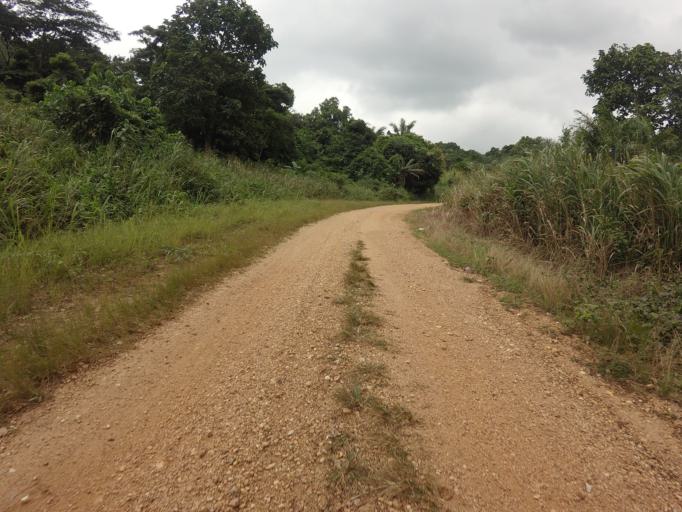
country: GH
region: Volta
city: Kpandu
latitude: 6.8727
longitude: 0.4276
